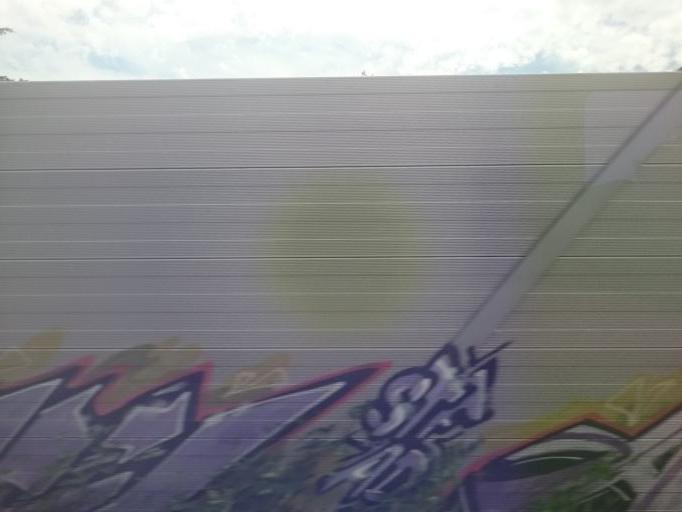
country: DE
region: Bavaria
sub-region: Upper Bavaria
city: Bogenhausen
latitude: 48.1329
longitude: 11.6424
